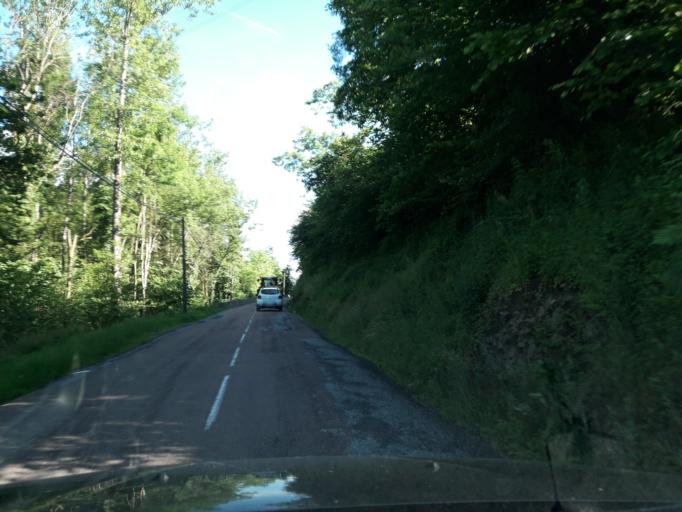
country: FR
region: Rhone-Alpes
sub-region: Departement de la Savoie
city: La Bridoire
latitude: 45.5378
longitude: 5.7613
